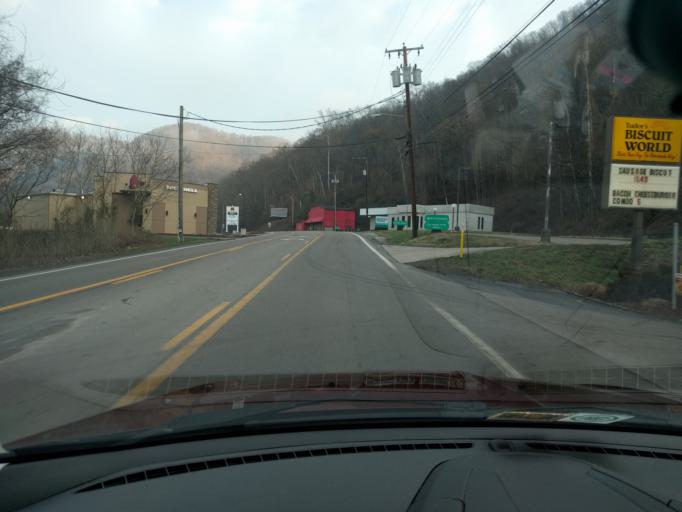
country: US
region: West Virginia
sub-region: Kanawha County
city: Montgomery
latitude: 38.1758
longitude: -81.3040
